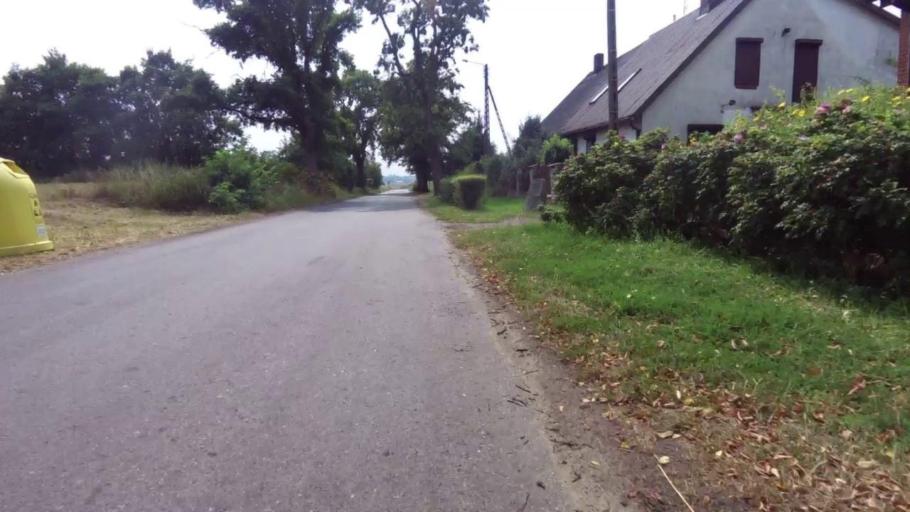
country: PL
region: West Pomeranian Voivodeship
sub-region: Powiat choszczenski
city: Choszczno
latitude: 53.1901
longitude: 15.3960
